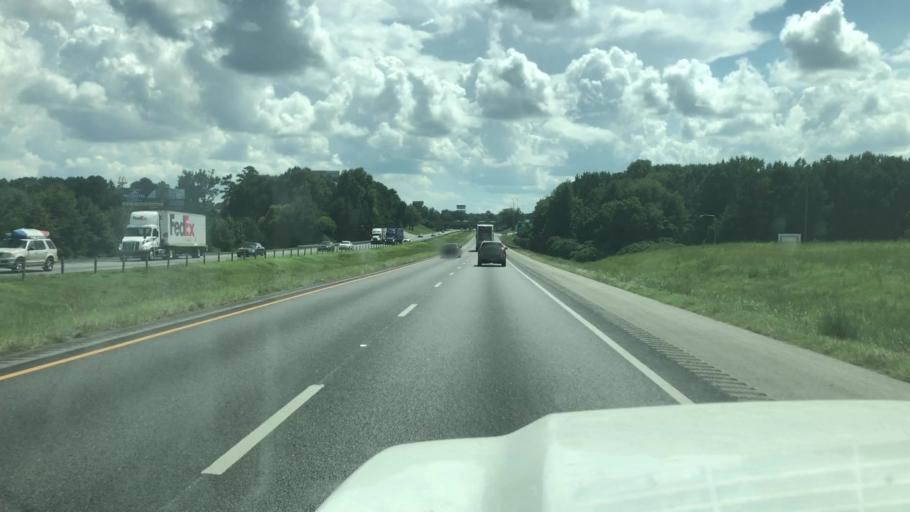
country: US
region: Alabama
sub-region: Lee County
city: Opelika
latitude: 32.6492
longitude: -85.3491
